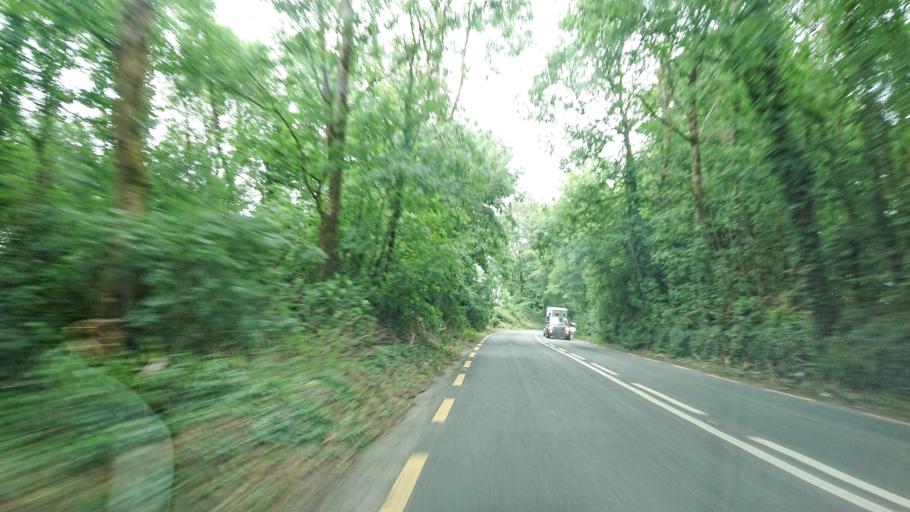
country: IE
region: Munster
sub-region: County Cork
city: Kanturk
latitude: 52.1244
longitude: -8.9761
